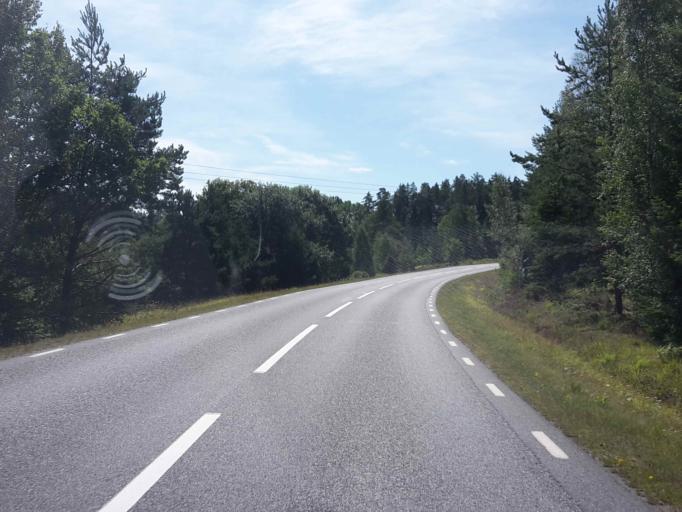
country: SE
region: OEstergoetland
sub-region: Atvidabergs Kommun
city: Atvidaberg
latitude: 58.1387
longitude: 15.9598
